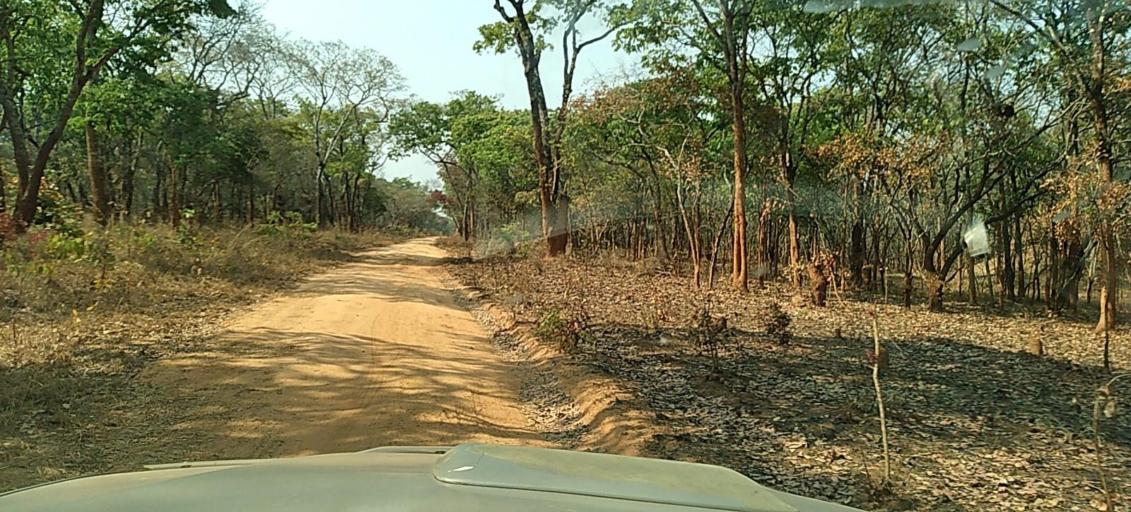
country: ZM
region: North-Western
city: Kasempa
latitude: -13.5300
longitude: 26.4090
